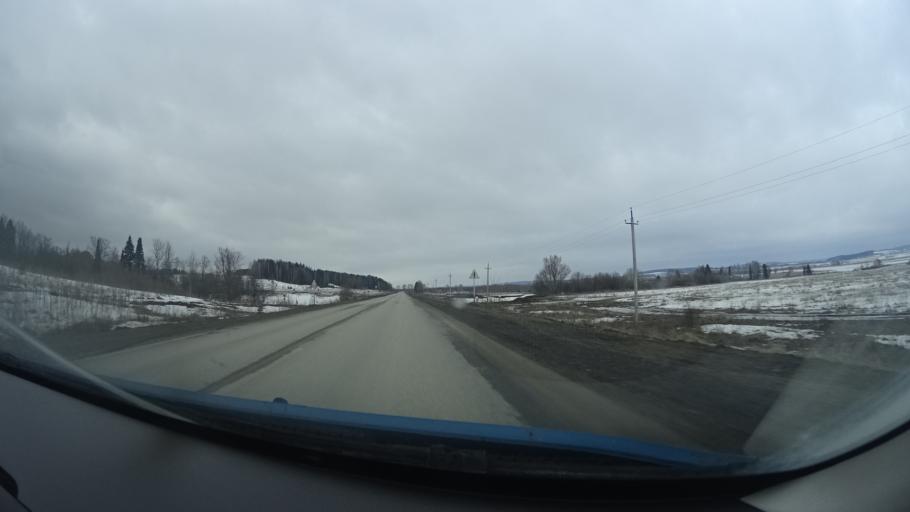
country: RU
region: Perm
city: Osa
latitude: 57.2159
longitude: 55.5918
